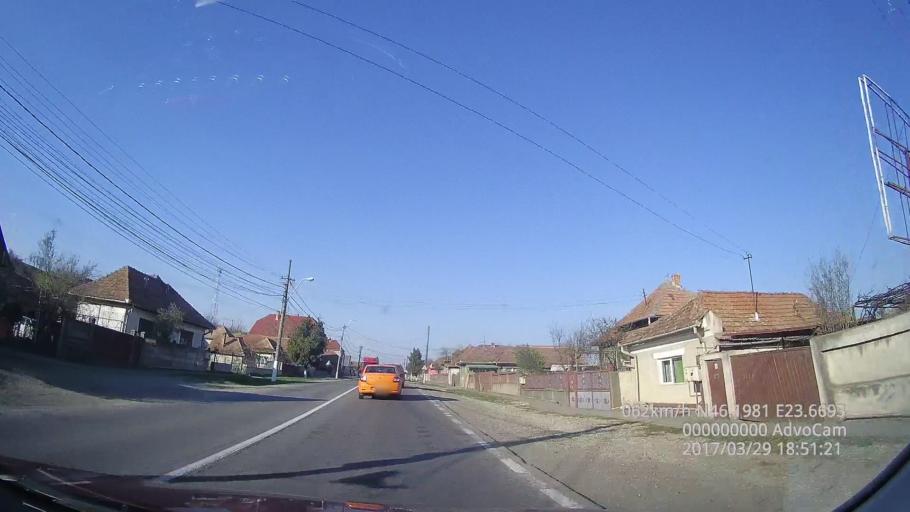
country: RO
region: Alba
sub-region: Oras Teius
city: Teius
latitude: 46.1982
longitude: 23.6693
